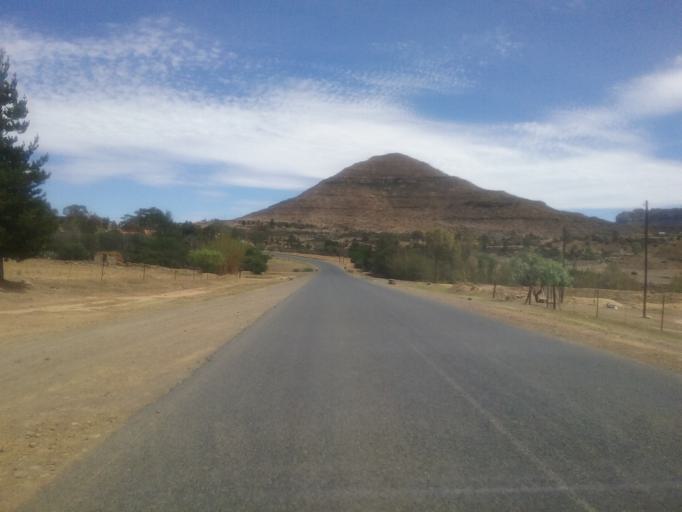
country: LS
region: Mafeteng
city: Mafeteng
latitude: -29.9564
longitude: 27.2884
